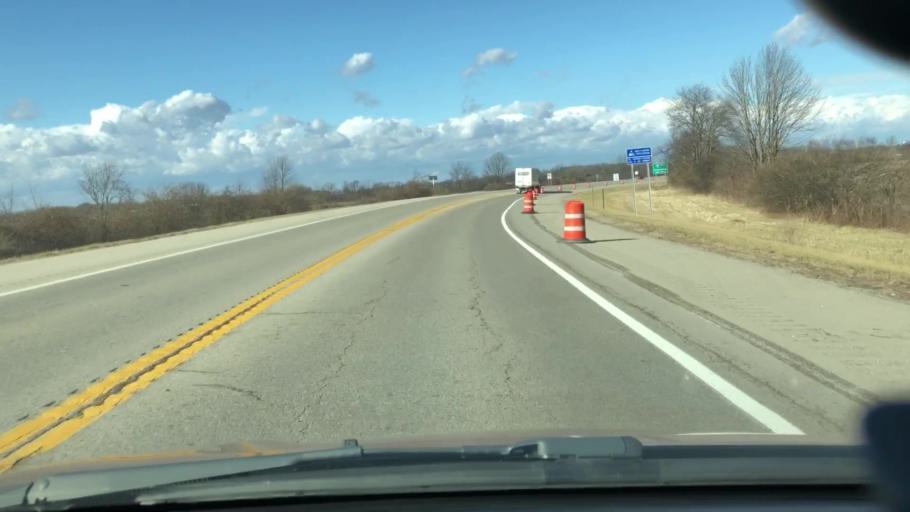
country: US
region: Ohio
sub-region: Clark County
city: Springfield
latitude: 39.8828
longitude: -83.8527
